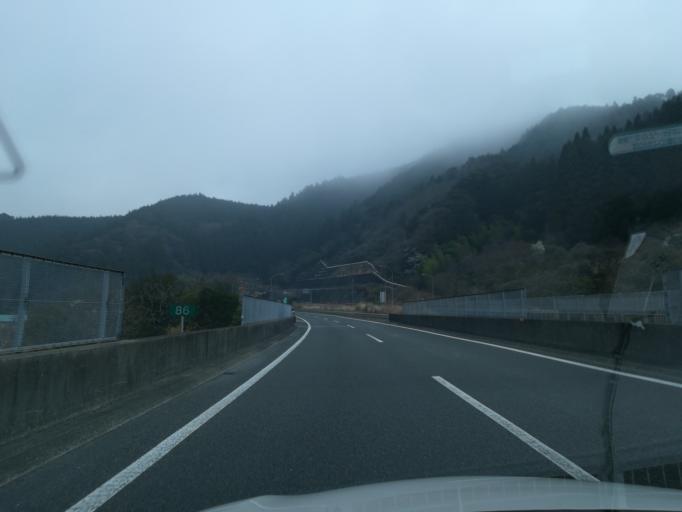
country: JP
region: Kochi
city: Kochi-shi
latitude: 33.7703
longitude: 133.6593
